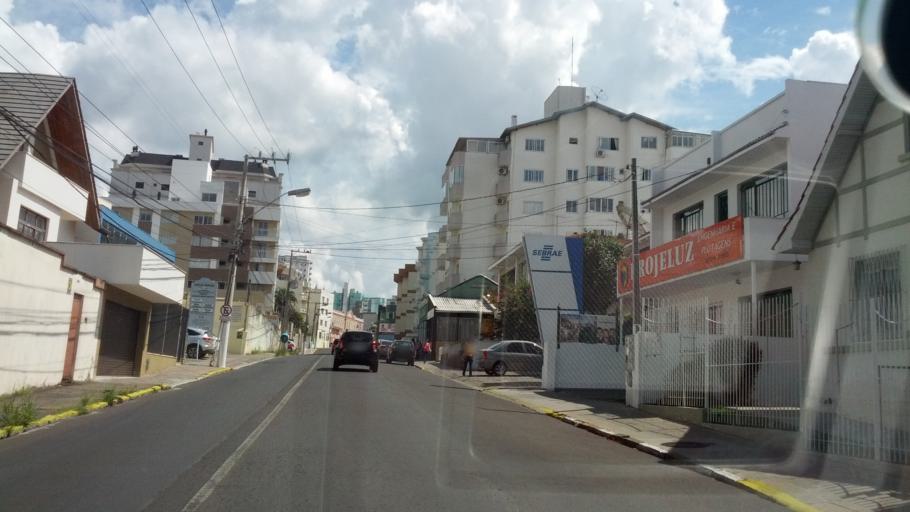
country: BR
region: Santa Catarina
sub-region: Lages
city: Lages
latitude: -27.8138
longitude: -50.3220
